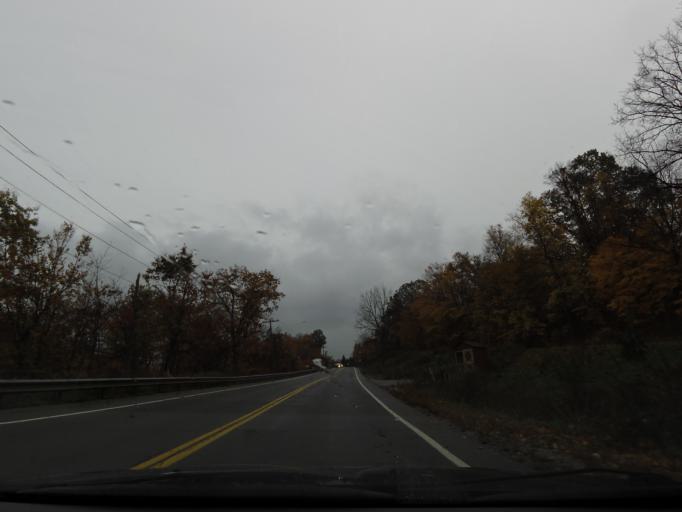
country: CA
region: Ontario
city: Burlington
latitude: 43.4240
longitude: -79.8311
